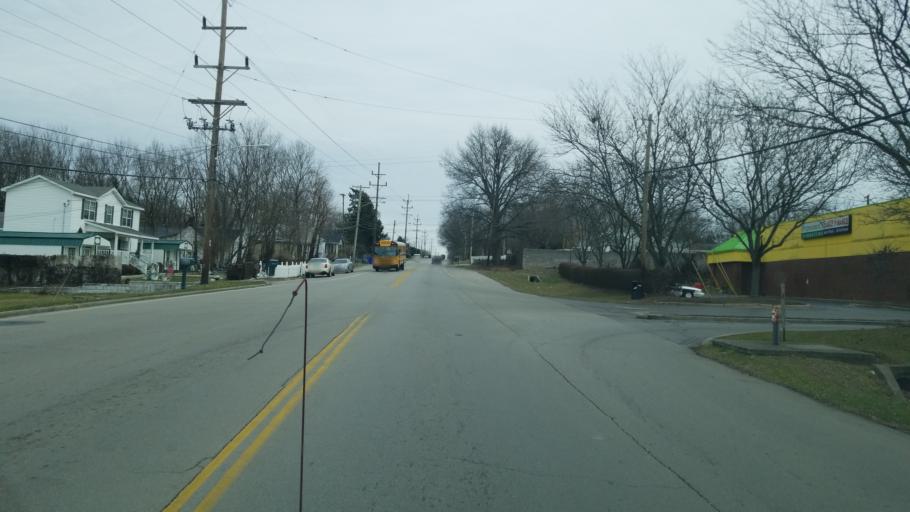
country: US
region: Kentucky
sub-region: Fayette County
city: Lexington-Fayette
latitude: 38.0657
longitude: -84.4695
